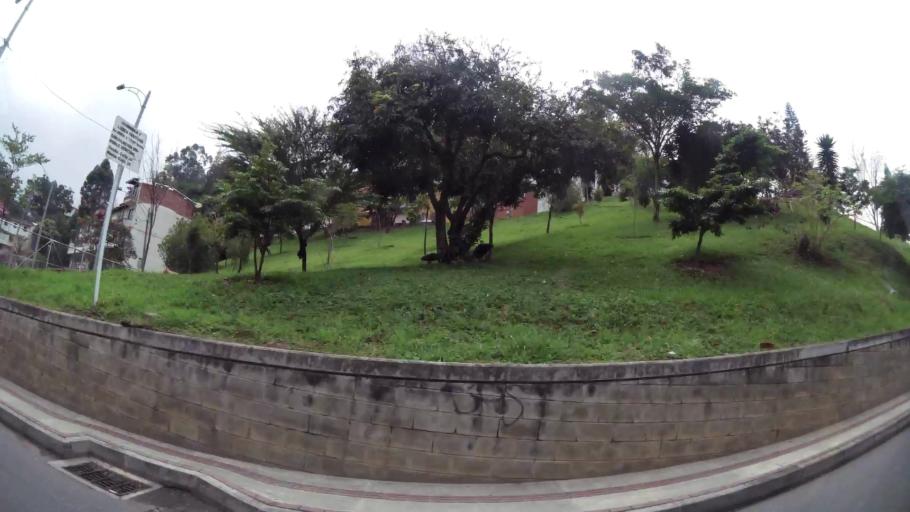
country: CO
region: Antioquia
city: Medellin
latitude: 6.2342
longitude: -75.5642
